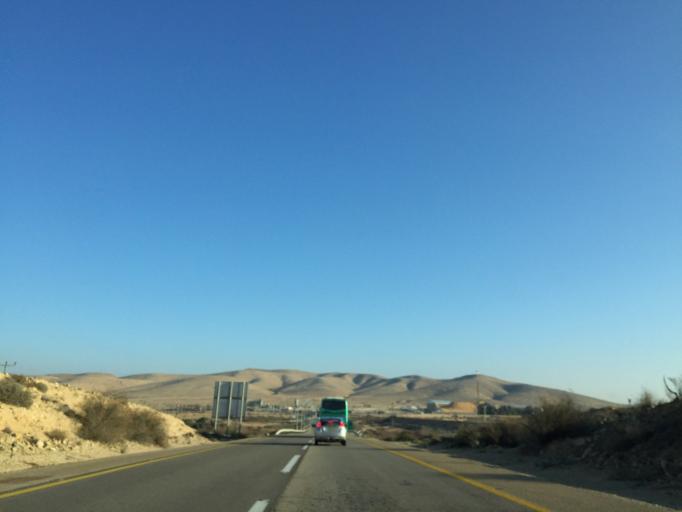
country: IL
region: Southern District
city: Dimona
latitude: 31.0622
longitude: 35.0028
